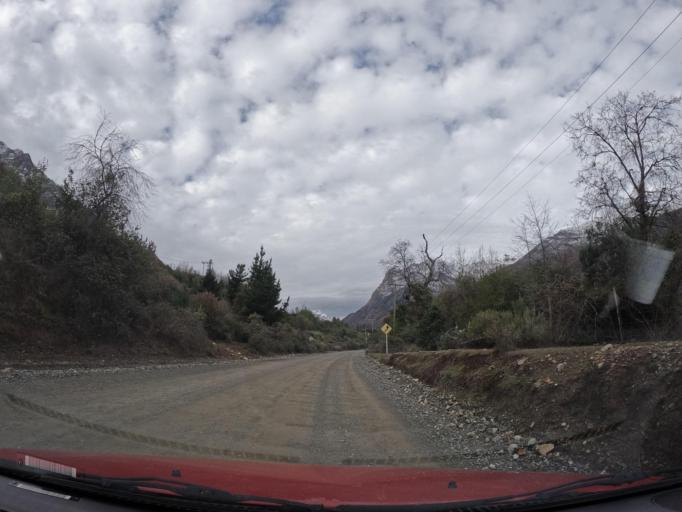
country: CL
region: Maule
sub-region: Provincia de Linares
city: Colbun
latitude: -35.8585
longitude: -71.2360
